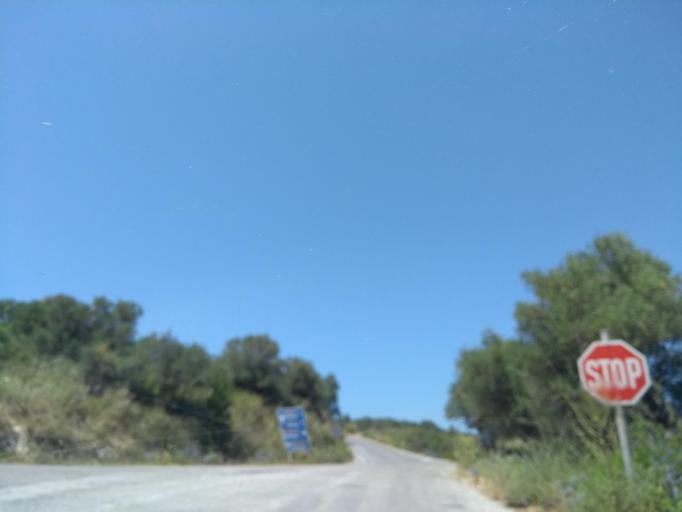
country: GR
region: Crete
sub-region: Nomos Chanias
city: Georgioupolis
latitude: 35.3194
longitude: 24.3123
